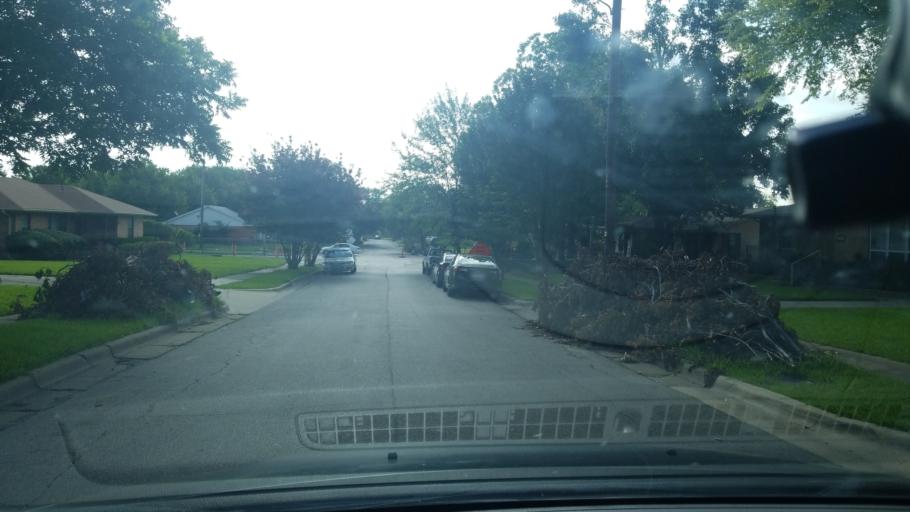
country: US
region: Texas
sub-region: Dallas County
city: Balch Springs
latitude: 32.7419
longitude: -96.6664
